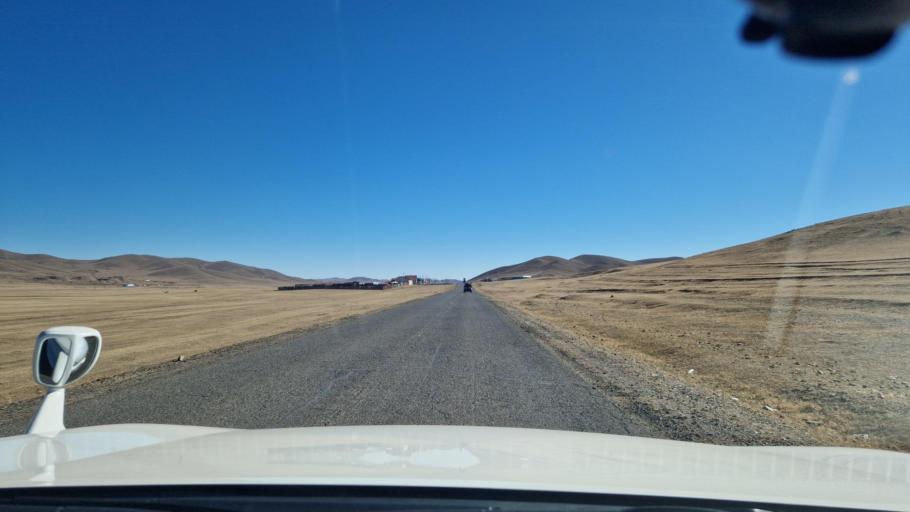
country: MN
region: Hentiy
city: Modot
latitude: 47.7279
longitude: 109.0179
